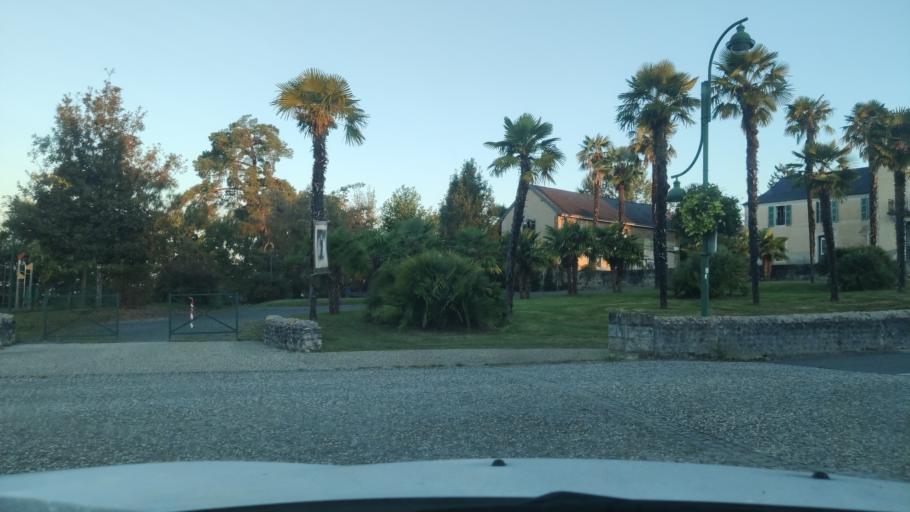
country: FR
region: Aquitaine
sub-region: Departement des Pyrenees-Atlantiques
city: Sauvagnon
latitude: 43.4021
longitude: -0.3872
